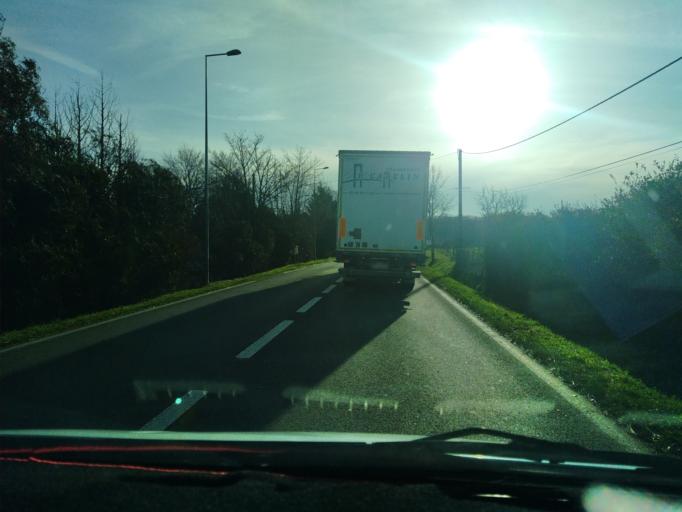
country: FR
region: Franche-Comte
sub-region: Departement de la Haute-Saone
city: Gray
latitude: 47.4322
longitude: 5.6034
